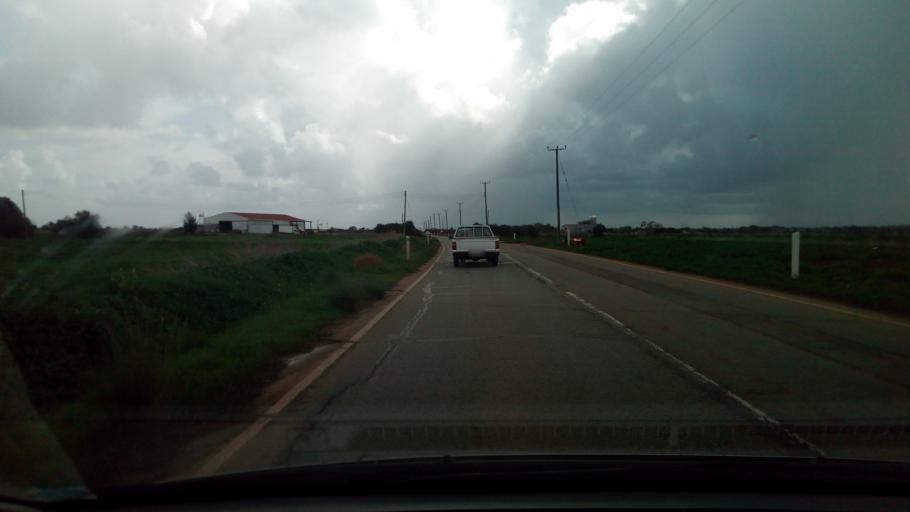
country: CY
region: Ammochostos
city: Liopetri
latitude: 34.9912
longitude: 33.8923
